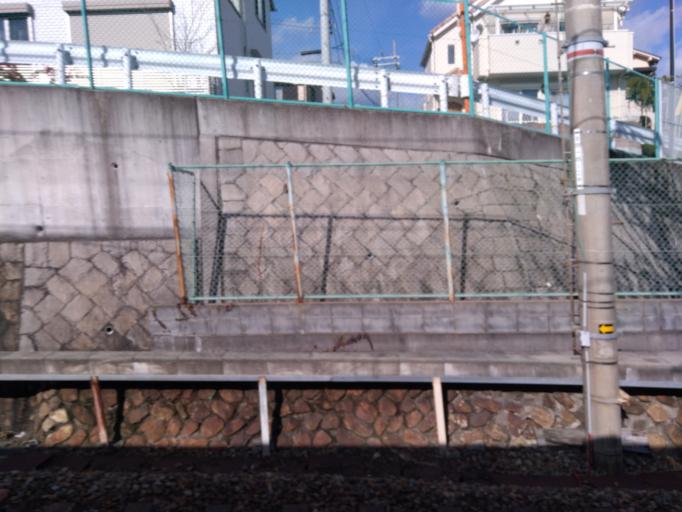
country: JP
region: Hyogo
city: Takarazuka
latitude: 34.8112
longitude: 135.3466
